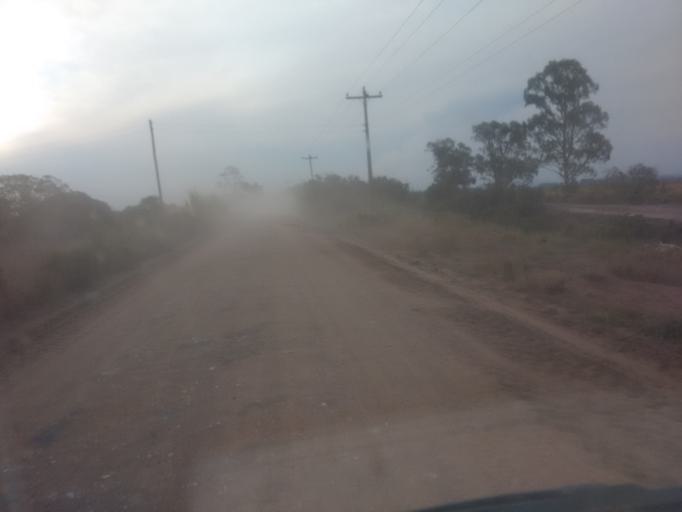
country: BR
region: Rio Grande do Sul
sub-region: Camaqua
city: Camaqua
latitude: -30.9330
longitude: -51.7877
